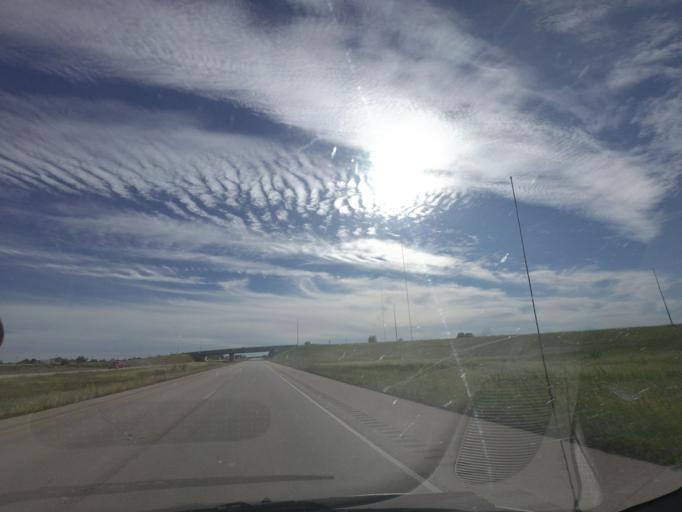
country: US
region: Illinois
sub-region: Piatt County
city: Cerro Gordo
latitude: 39.9574
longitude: -88.8213
